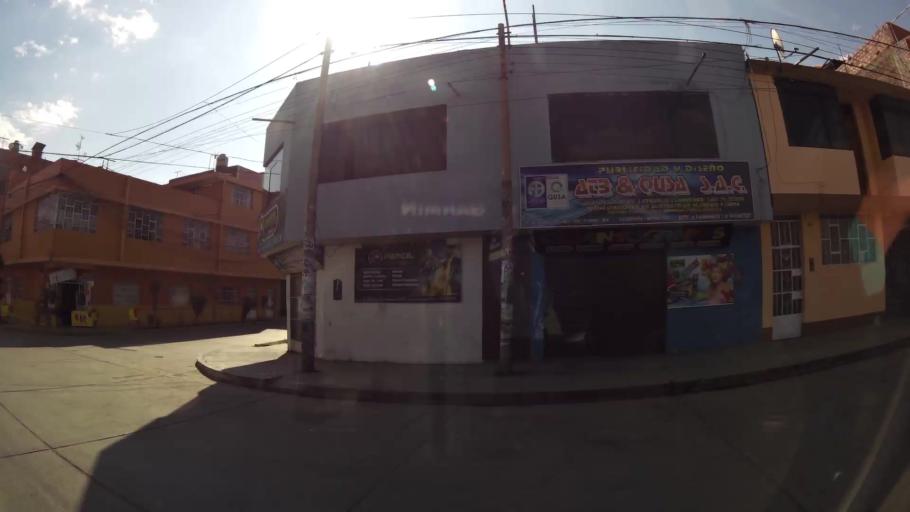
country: PE
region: Junin
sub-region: Provincia de Huancayo
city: El Tambo
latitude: -12.0635
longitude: -75.2177
